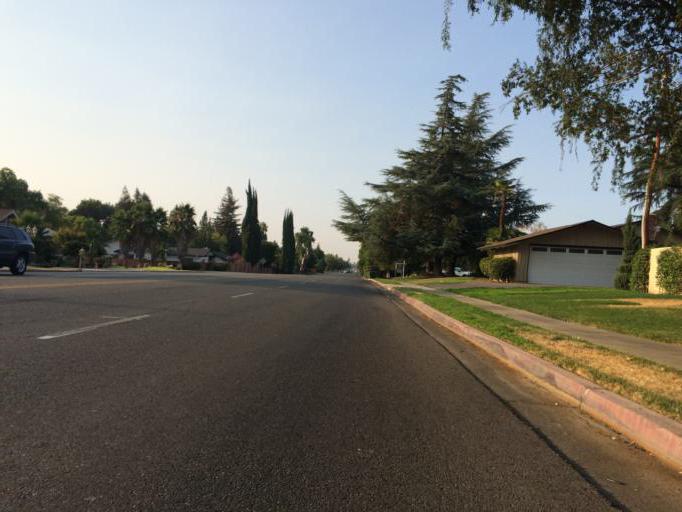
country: US
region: California
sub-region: Fresno County
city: Fresno
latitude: 36.8193
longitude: -119.8173
